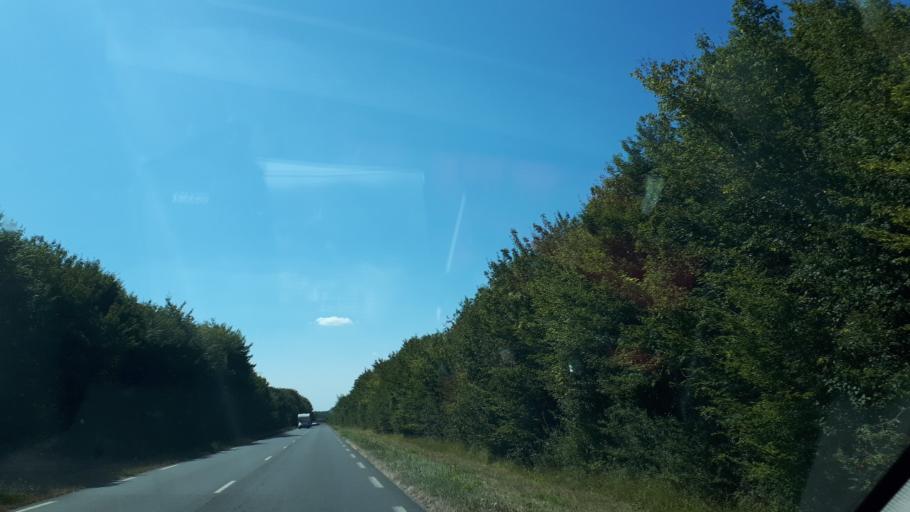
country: FR
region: Centre
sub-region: Departement du Loir-et-Cher
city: Vineuil
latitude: 47.5617
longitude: 1.3847
